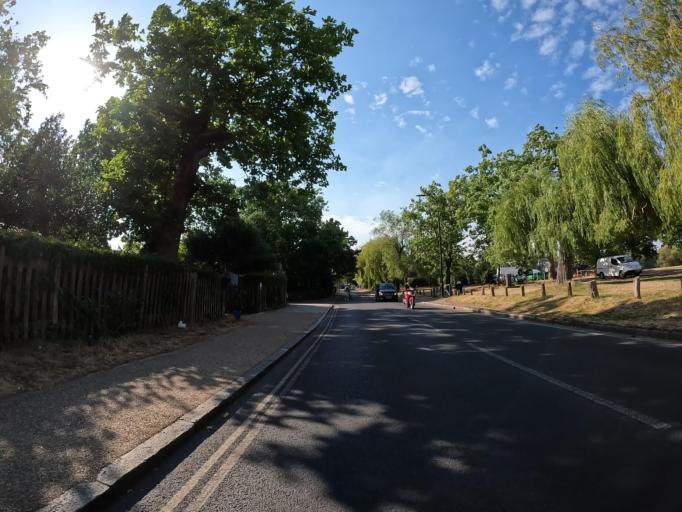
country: GB
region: England
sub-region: Greater London
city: Hadley Wood
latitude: 51.6790
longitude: -0.1625
